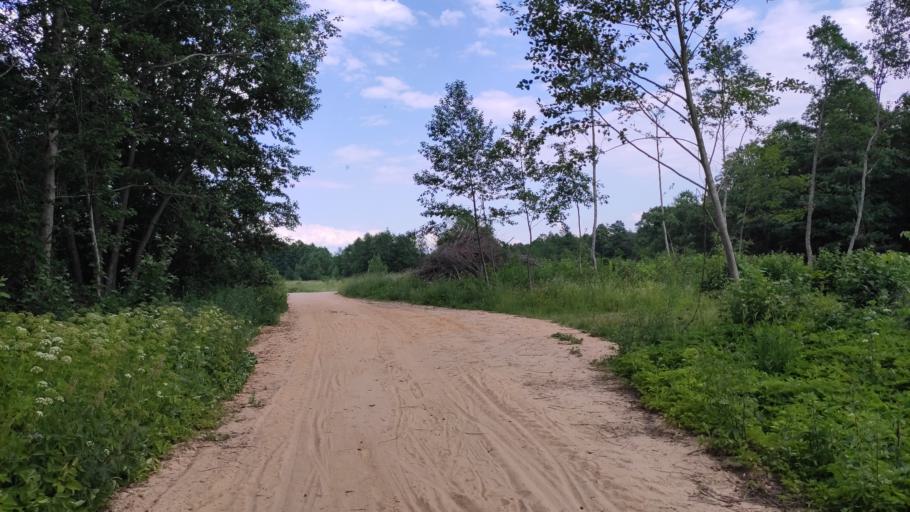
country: BY
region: Grodnenskaya
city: Ashmyany
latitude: 54.4195
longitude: 25.9129
